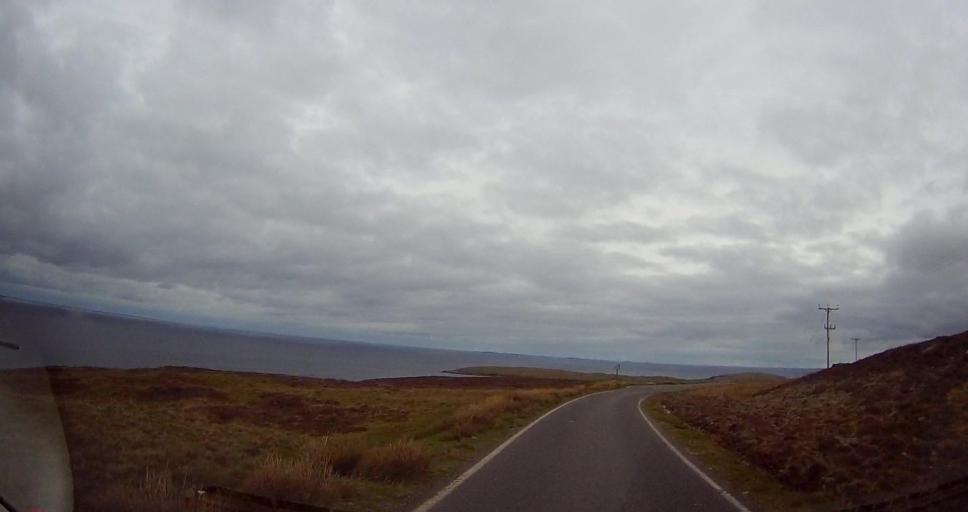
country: GB
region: Scotland
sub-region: Shetland Islands
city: Shetland
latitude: 60.5436
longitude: -1.0541
